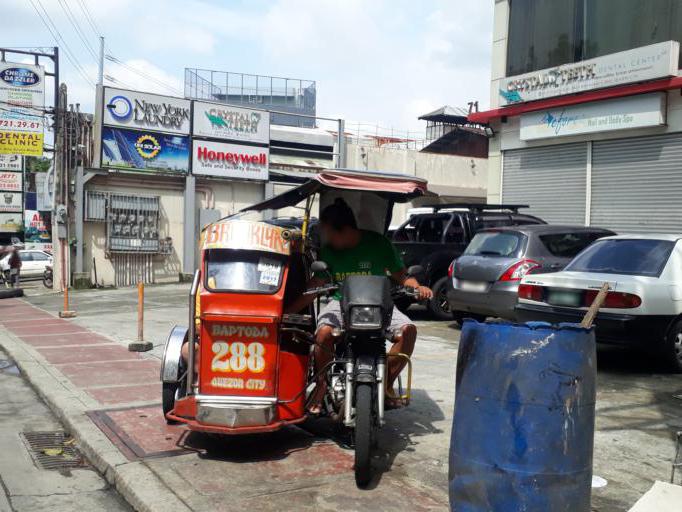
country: PH
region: Metro Manila
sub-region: San Juan
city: San Juan
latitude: 14.6149
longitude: 121.0493
